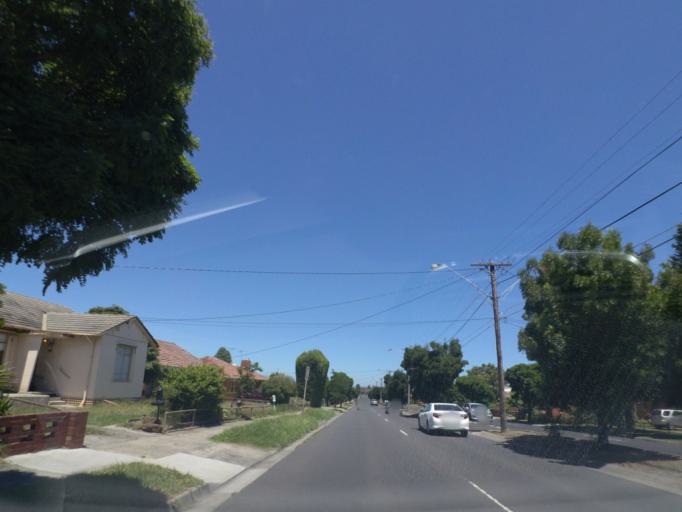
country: AU
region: Victoria
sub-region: Darebin
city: Preston
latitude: -37.7365
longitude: 145.0241
